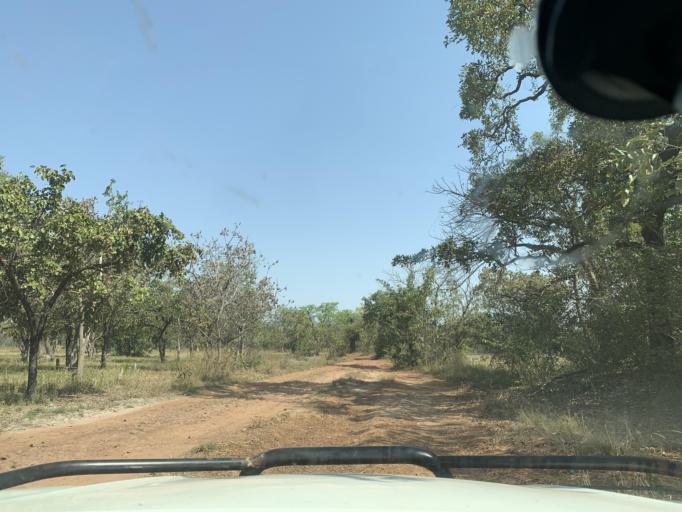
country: ML
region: Sikasso
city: Kolondieba
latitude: 10.8851
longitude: -6.7611
